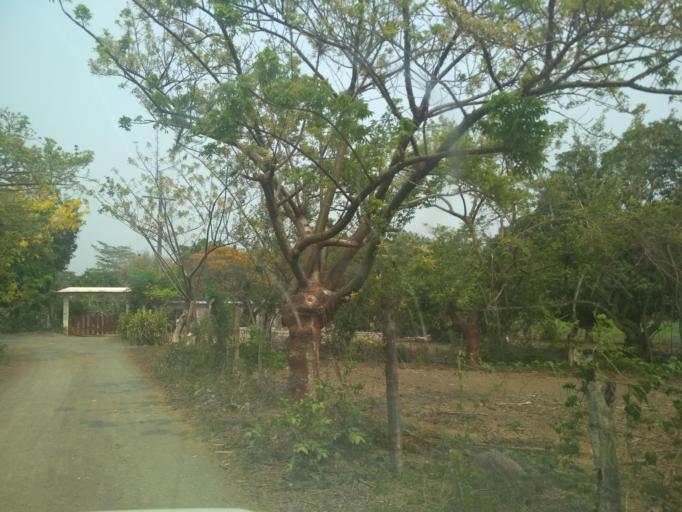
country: MX
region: Veracruz
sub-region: Veracruz
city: Delfino Victoria (Santa Fe)
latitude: 19.1766
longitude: -96.3215
